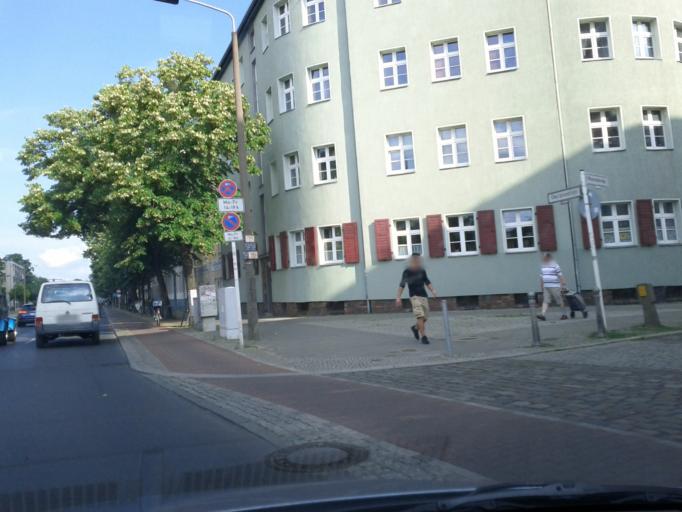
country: DE
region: Berlin
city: Kopenick Bezirk
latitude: 52.4456
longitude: 13.5636
